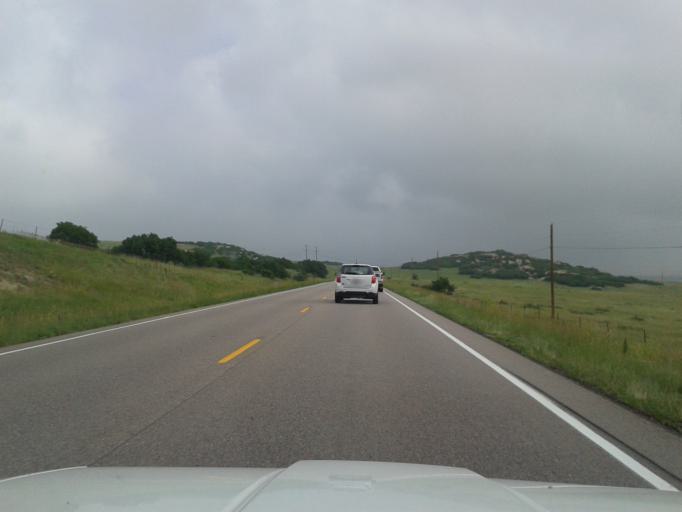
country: US
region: Colorado
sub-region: Douglas County
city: Castle Rock
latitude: 39.2776
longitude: -104.7369
